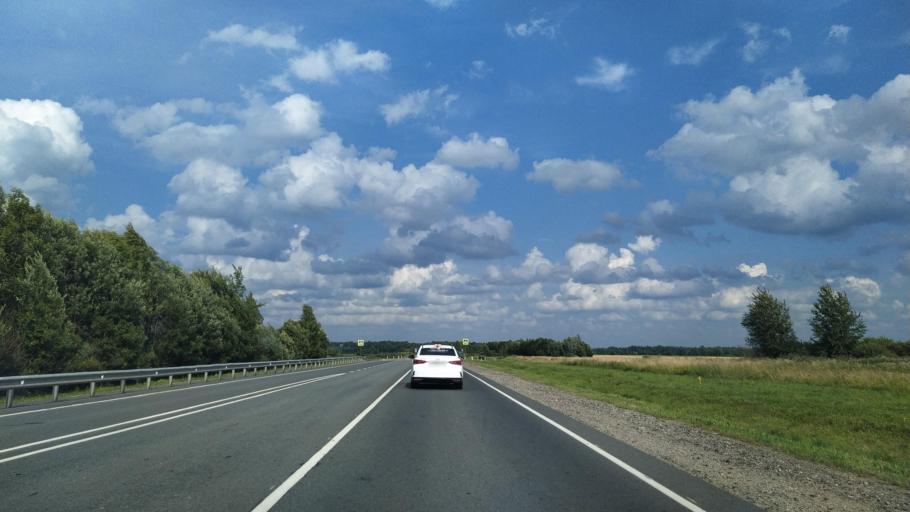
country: RU
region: Novgorod
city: Sol'tsy
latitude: 58.1346
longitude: 30.3847
